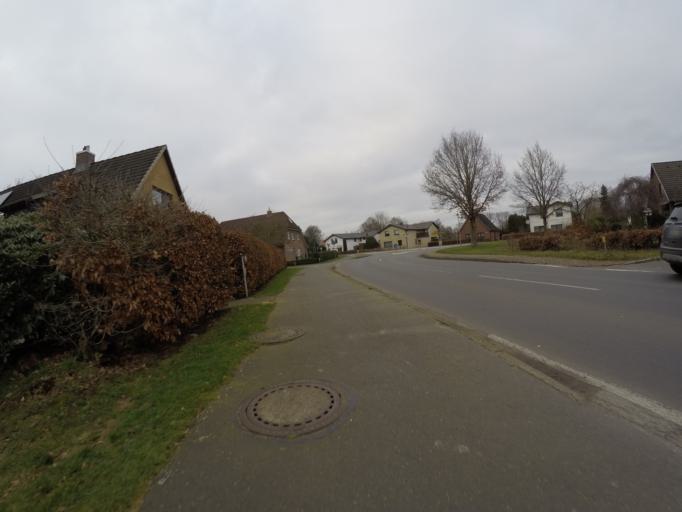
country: DE
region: Schleswig-Holstein
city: Hemdingen
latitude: 53.7658
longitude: 9.8473
